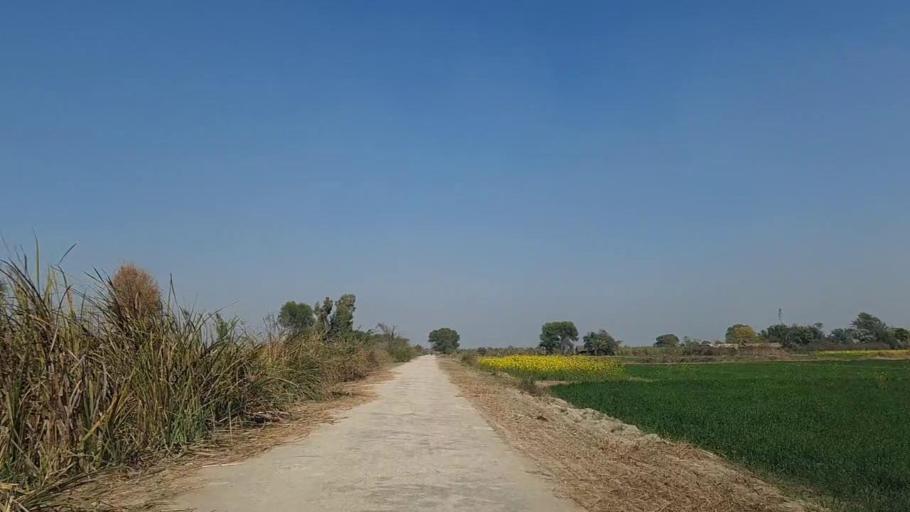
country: PK
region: Sindh
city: Daur
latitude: 26.5005
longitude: 68.3463
